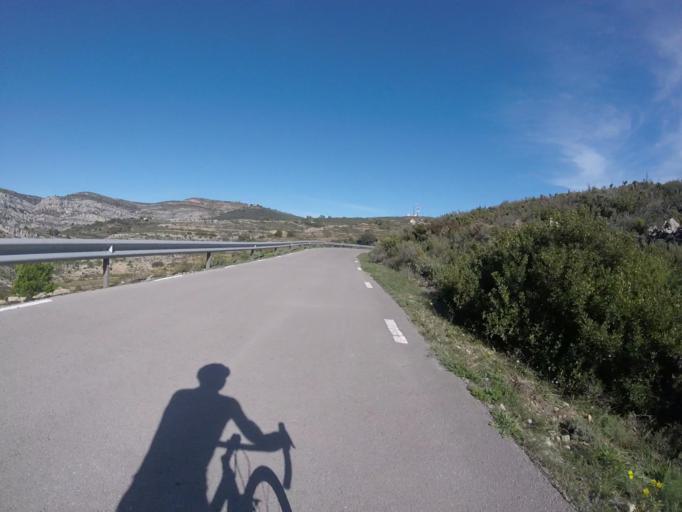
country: ES
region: Valencia
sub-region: Provincia de Castello
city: Sarratella
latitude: 40.2940
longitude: 0.0308
